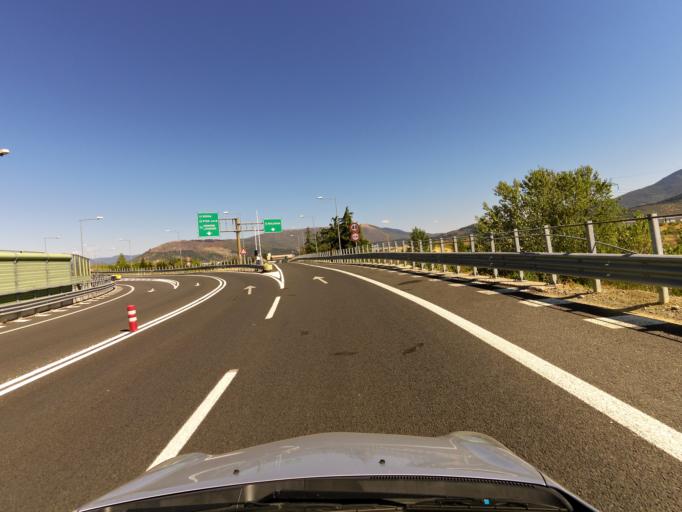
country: IT
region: Tuscany
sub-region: Province of Florence
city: Calenzano
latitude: 43.8365
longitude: 11.1629
